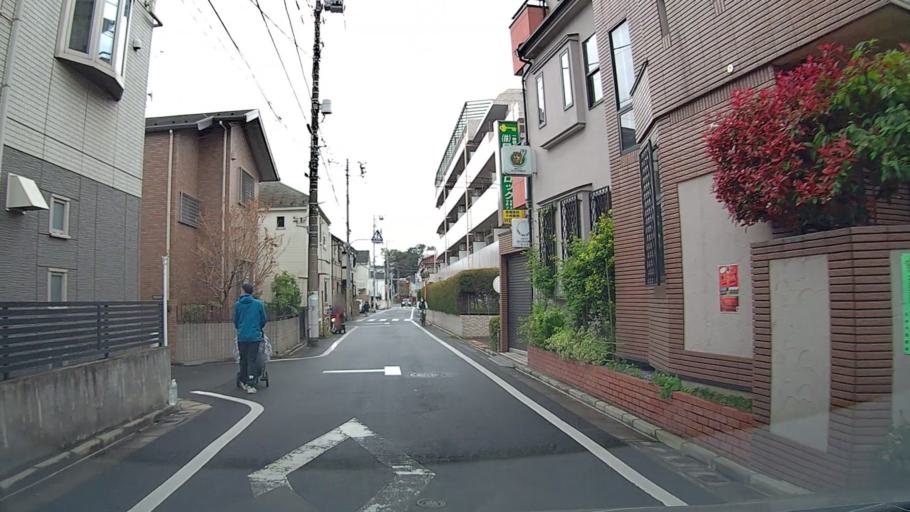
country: JP
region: Tokyo
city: Musashino
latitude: 35.7399
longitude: 139.5816
